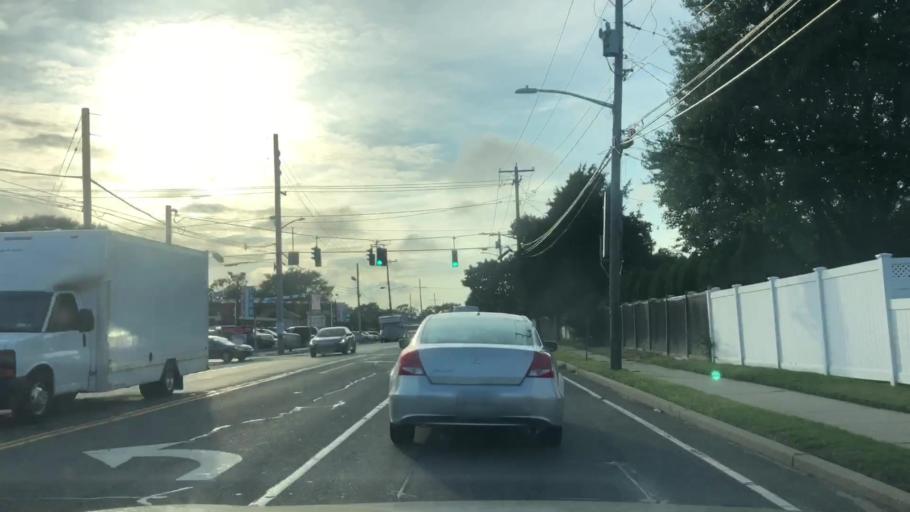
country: US
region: New York
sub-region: Nassau County
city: Massapequa
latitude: 40.6912
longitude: -73.4846
